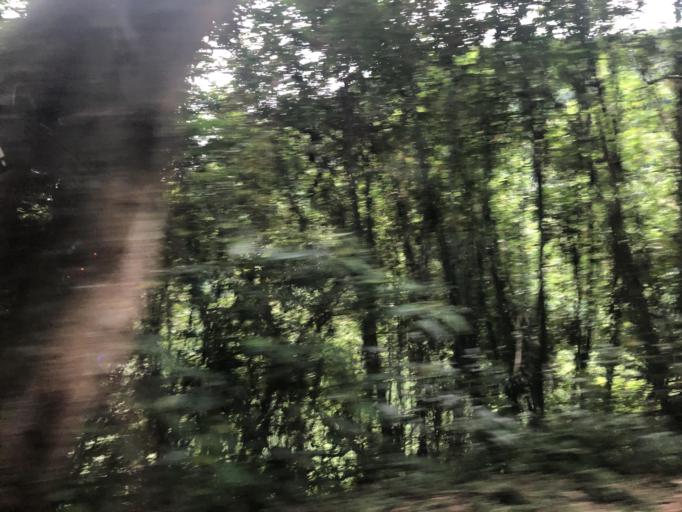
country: TW
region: Taipei
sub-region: Taipei
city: Banqiao
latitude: 24.8932
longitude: 121.4285
